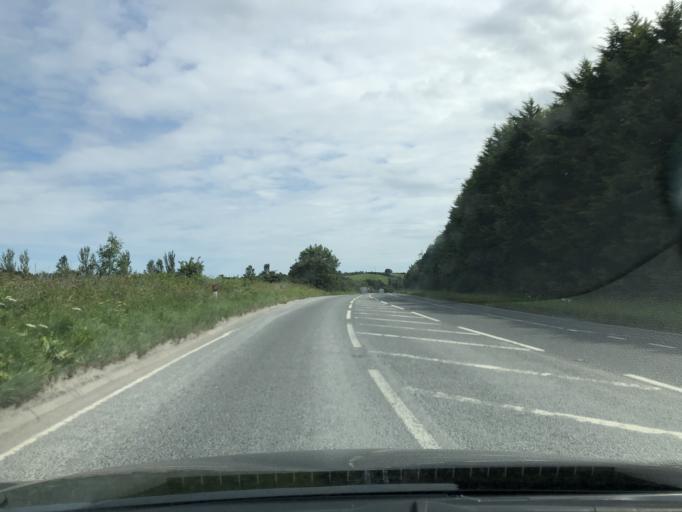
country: GB
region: Northern Ireland
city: Ballynahinch
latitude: 54.3383
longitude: -5.8379
